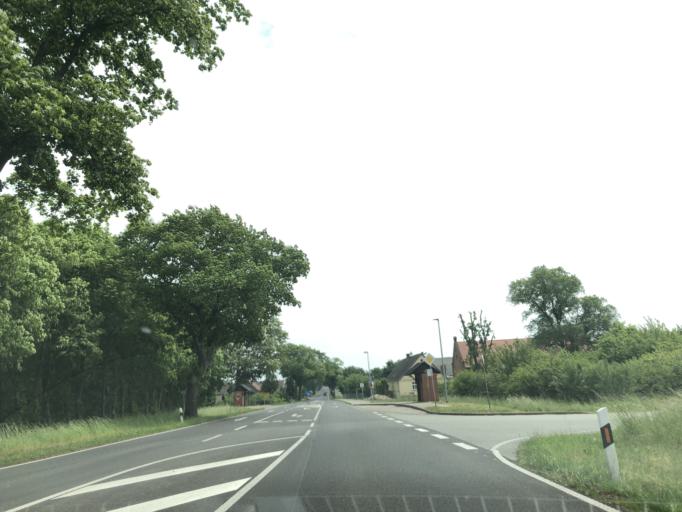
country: DE
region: Brandenburg
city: Kyritz
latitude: 52.9623
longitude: 12.3374
